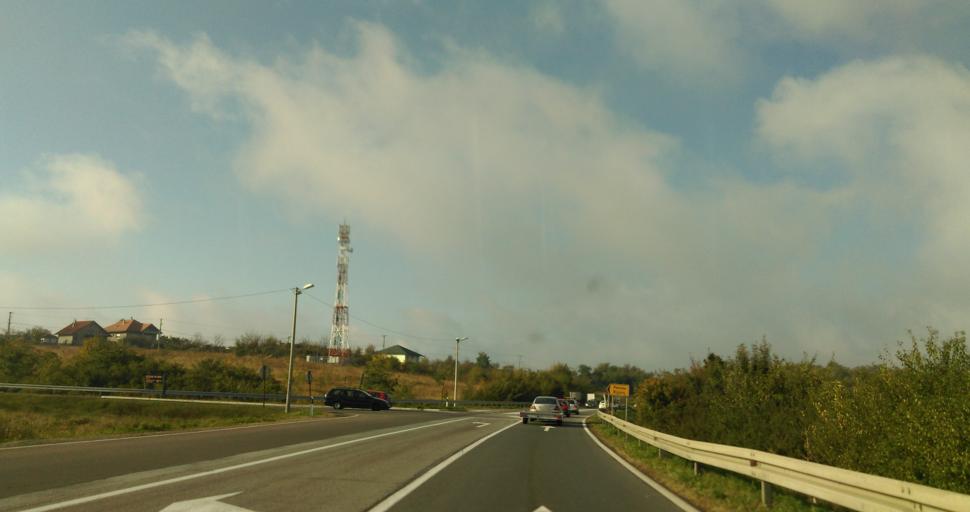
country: RS
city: Rusanj
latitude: 44.6516
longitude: 20.4294
